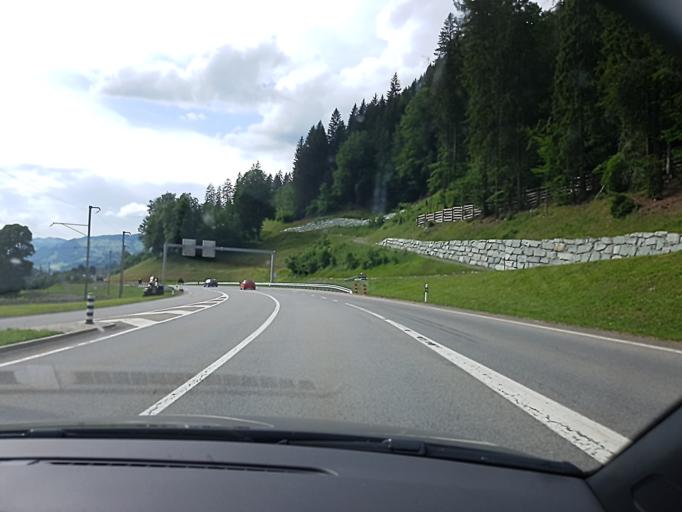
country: CH
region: Grisons
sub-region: Praettigau/Davos District
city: Klosters Serneus
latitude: 46.8899
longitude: 9.8526
